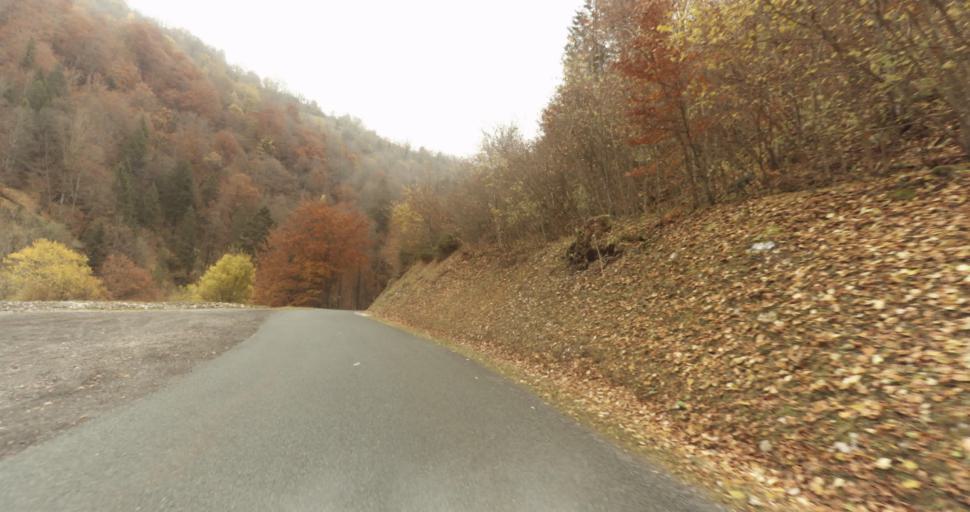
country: FR
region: Rhone-Alpes
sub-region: Departement de la Haute-Savoie
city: Doussard
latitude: 45.7874
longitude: 6.2590
